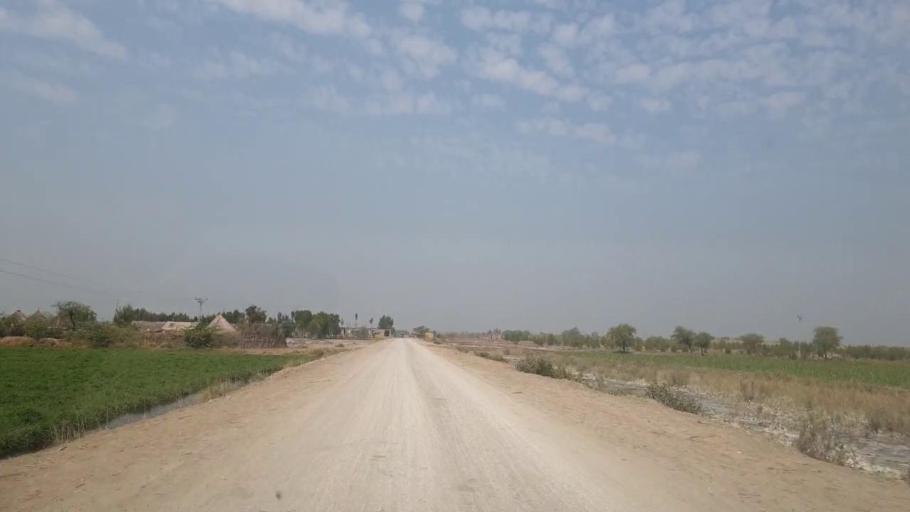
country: PK
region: Sindh
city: Mirpur Khas
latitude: 25.5489
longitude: 69.0799
